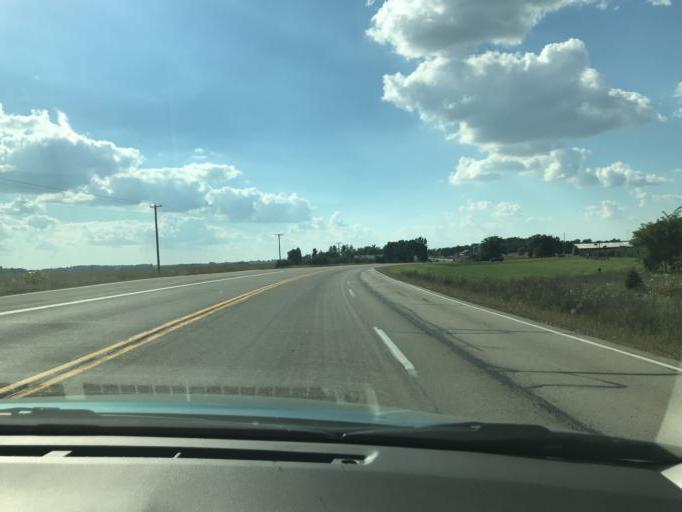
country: US
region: Wisconsin
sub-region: Green County
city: Brodhead
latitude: 42.5867
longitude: -89.4067
